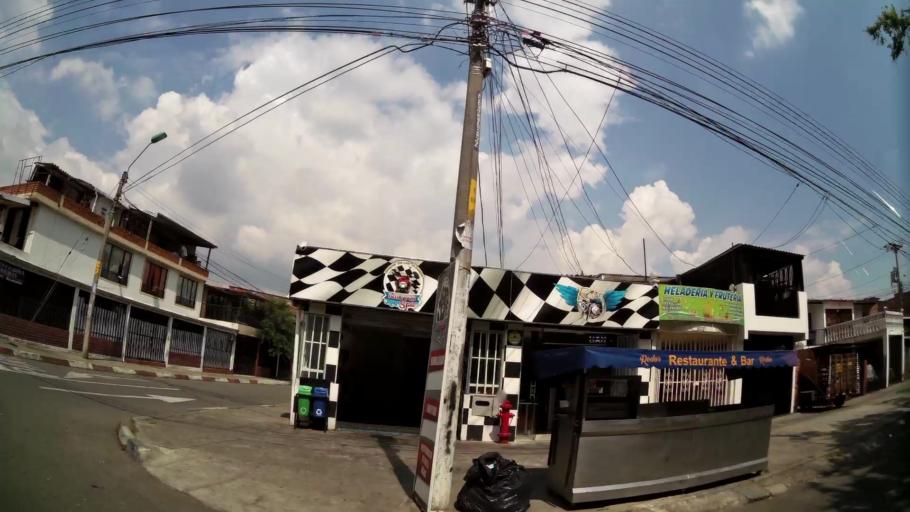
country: CO
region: Valle del Cauca
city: Cali
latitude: 3.4919
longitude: -76.5018
